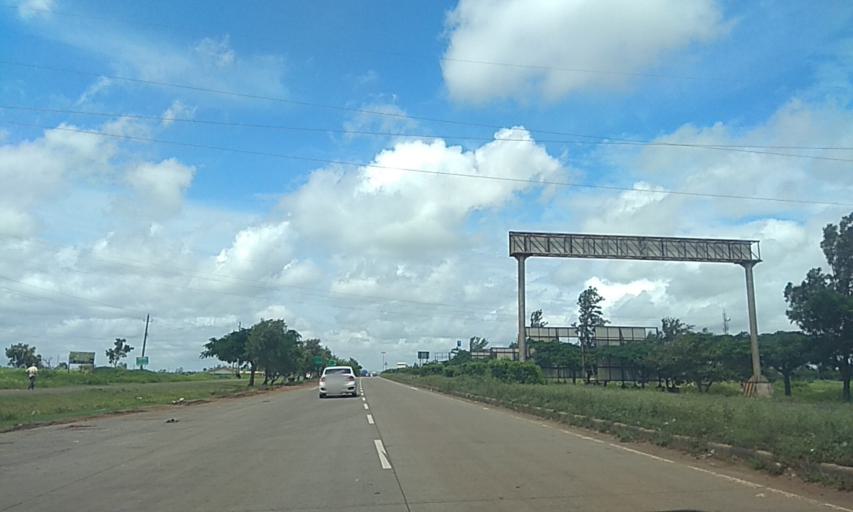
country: IN
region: Karnataka
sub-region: Belgaum
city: Sankeshwar
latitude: 16.1451
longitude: 74.5170
